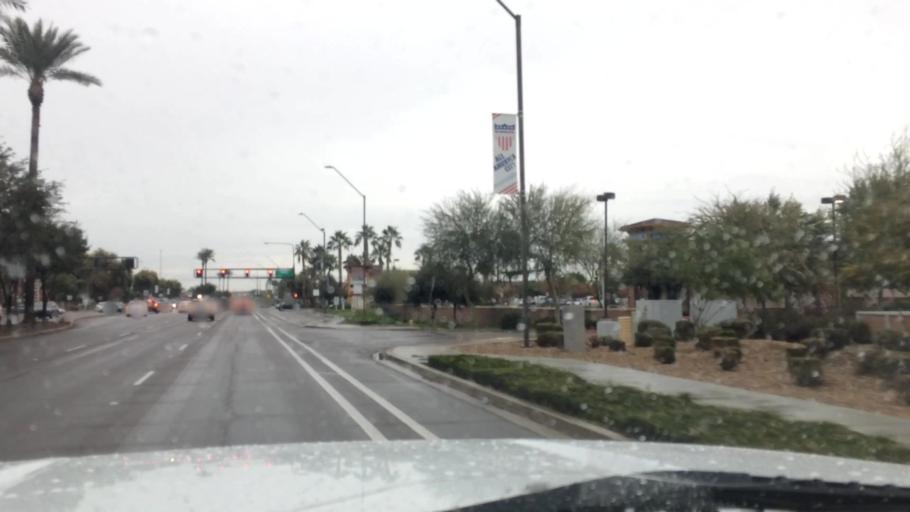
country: US
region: Arizona
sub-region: Maricopa County
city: Tolleson
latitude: 33.4646
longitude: -112.2785
